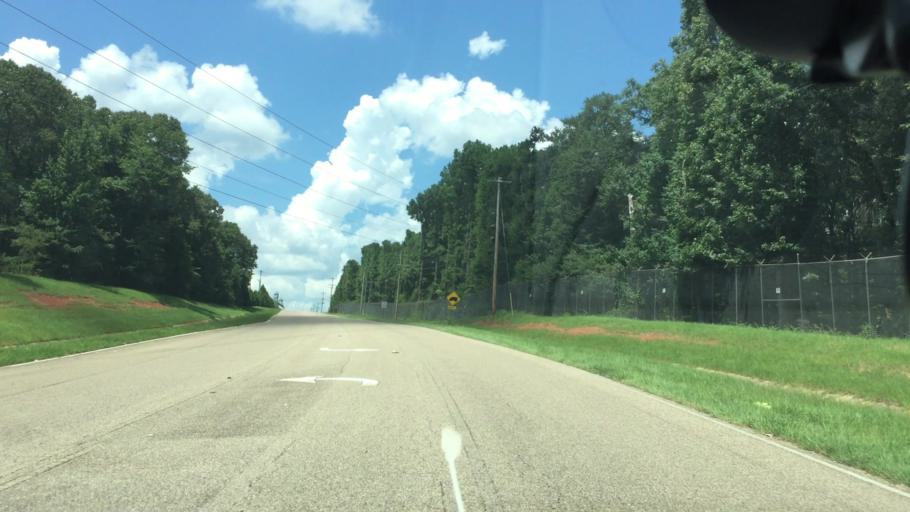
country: US
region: Alabama
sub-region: Pike County
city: Troy
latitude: 31.7765
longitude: -85.9783
